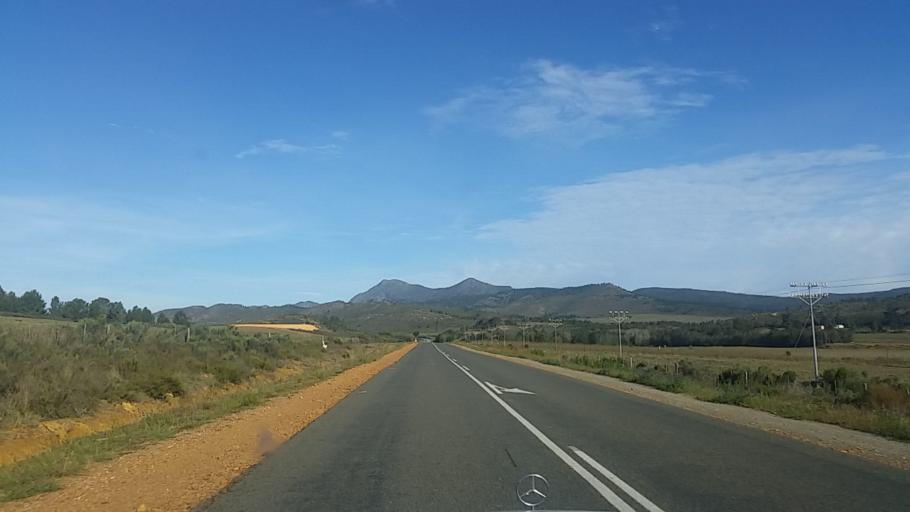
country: ZA
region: Western Cape
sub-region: Eden District Municipality
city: Knysna
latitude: -33.7659
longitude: 22.8902
